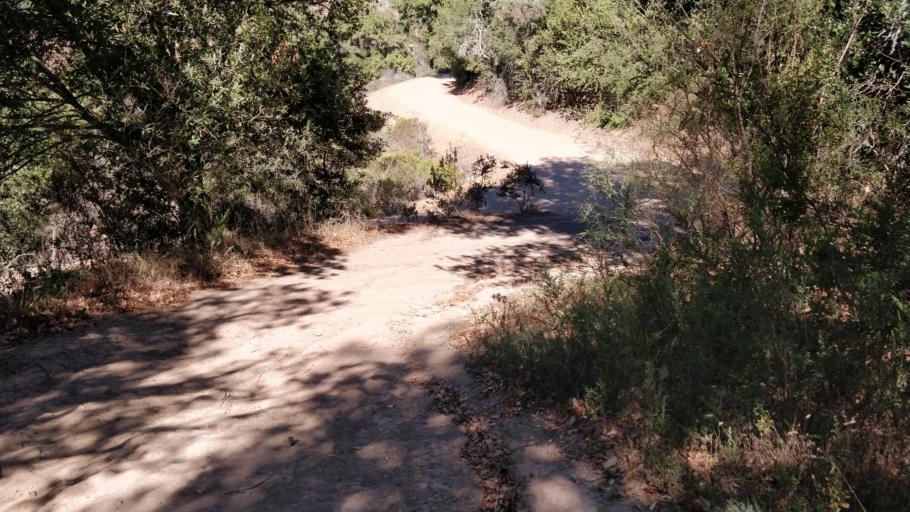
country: US
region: California
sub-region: Alameda County
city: Berkeley
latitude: 37.8745
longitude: -122.2281
